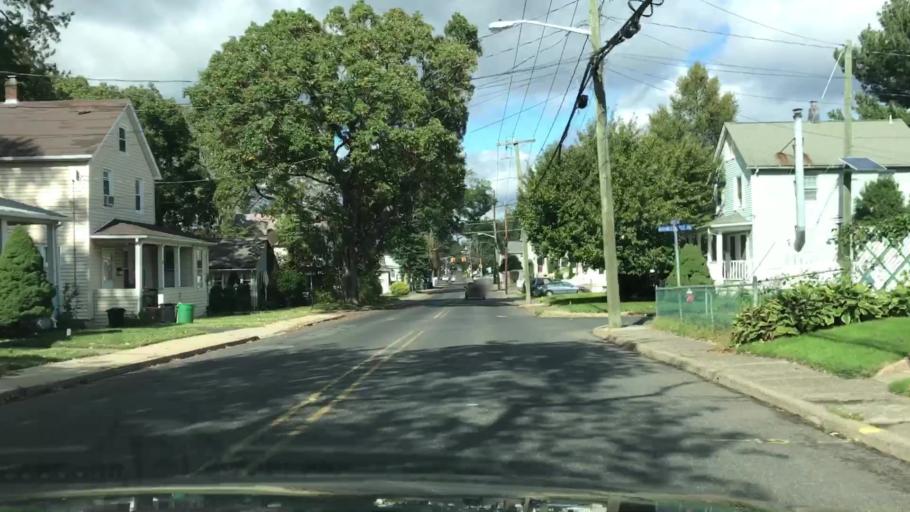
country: US
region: New Jersey
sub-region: Bergen County
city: Dumont
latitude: 40.9383
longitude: -74.0034
